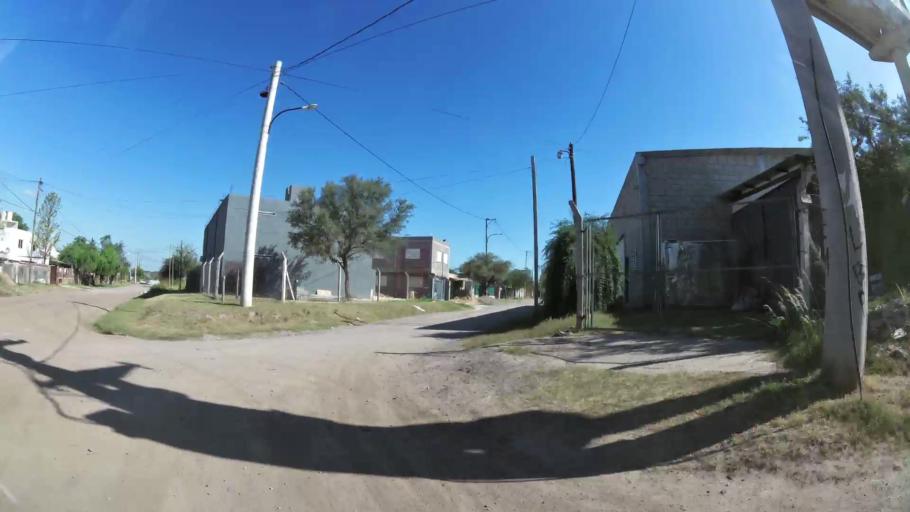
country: AR
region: Cordoba
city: La Calera
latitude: -31.3579
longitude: -64.3126
